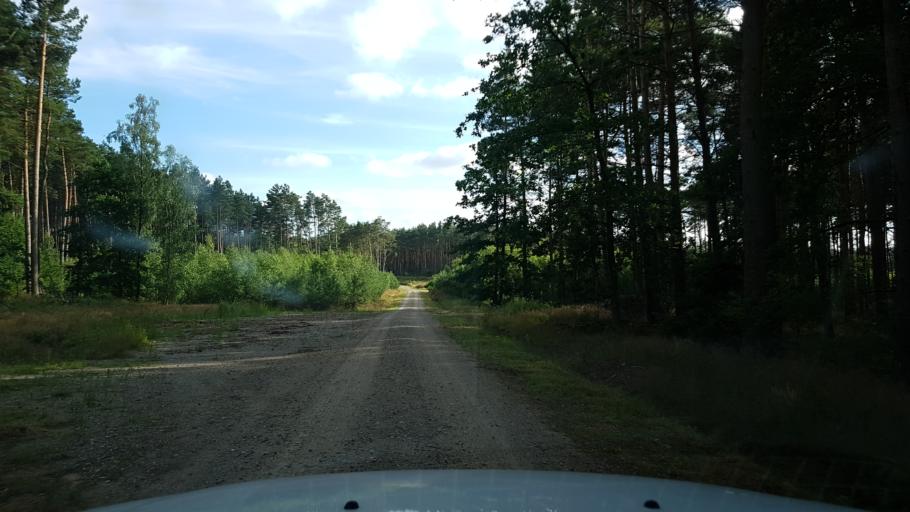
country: PL
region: West Pomeranian Voivodeship
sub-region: Powiat kolobrzeski
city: Grzybowo
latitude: 54.0981
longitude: 15.5360
